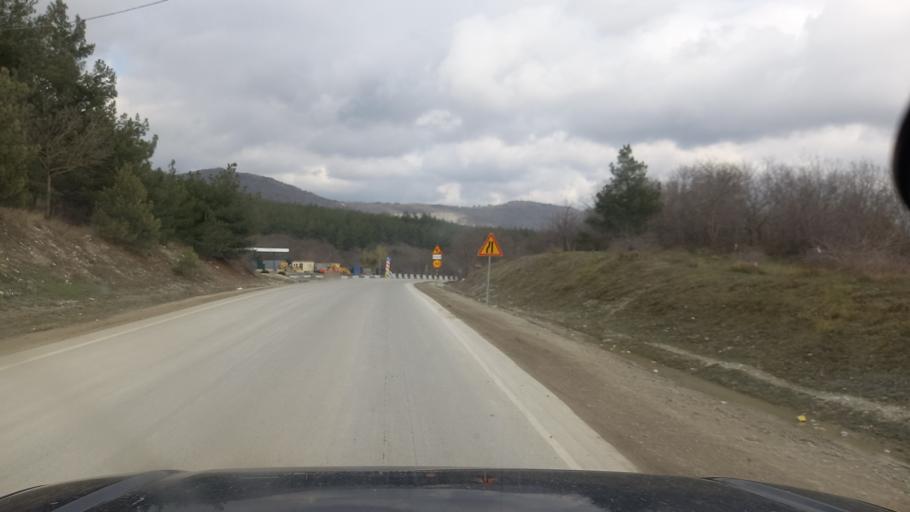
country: RU
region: Krasnodarskiy
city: Gelendzhik
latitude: 44.5549
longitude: 38.1231
